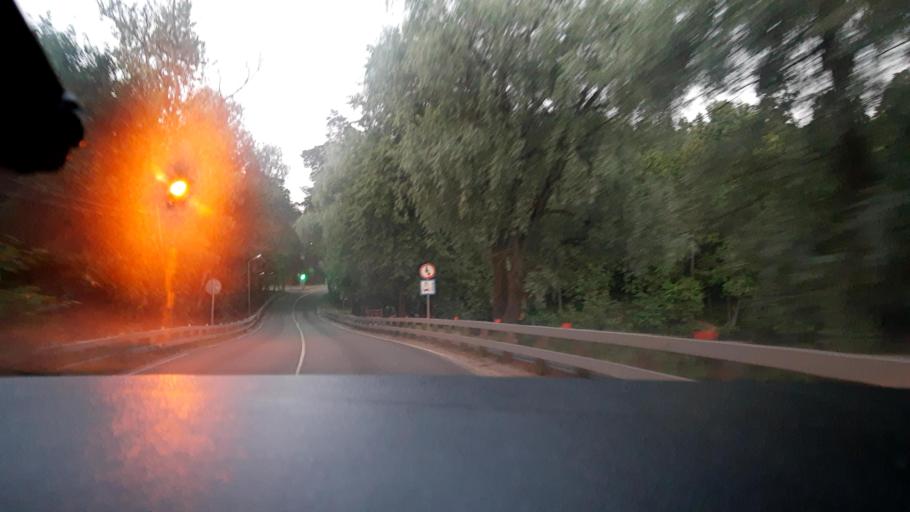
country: RU
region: Moscow
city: Novo-Peredelkino
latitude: 55.6641
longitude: 37.3285
